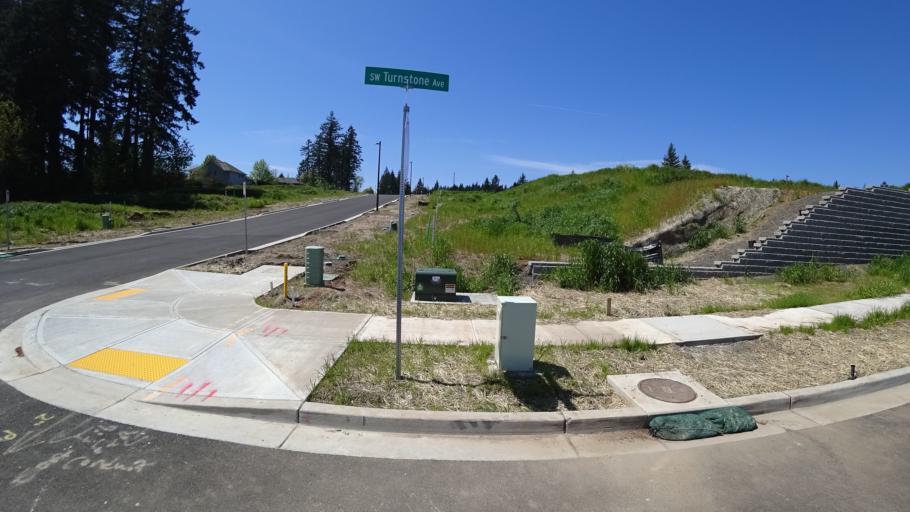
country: US
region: Oregon
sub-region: Washington County
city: King City
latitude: 45.4350
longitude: -122.8393
